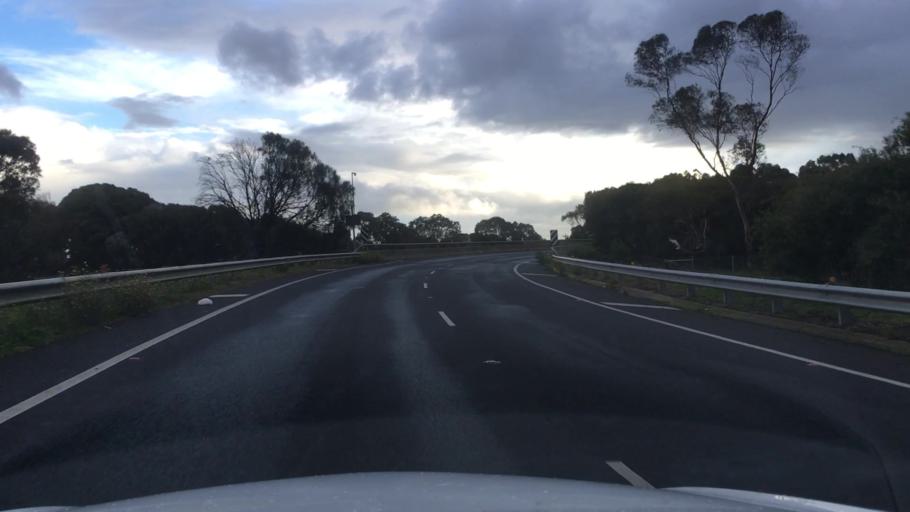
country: AU
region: Victoria
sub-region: Monash
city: Notting Hill
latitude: -37.9044
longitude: 145.1565
